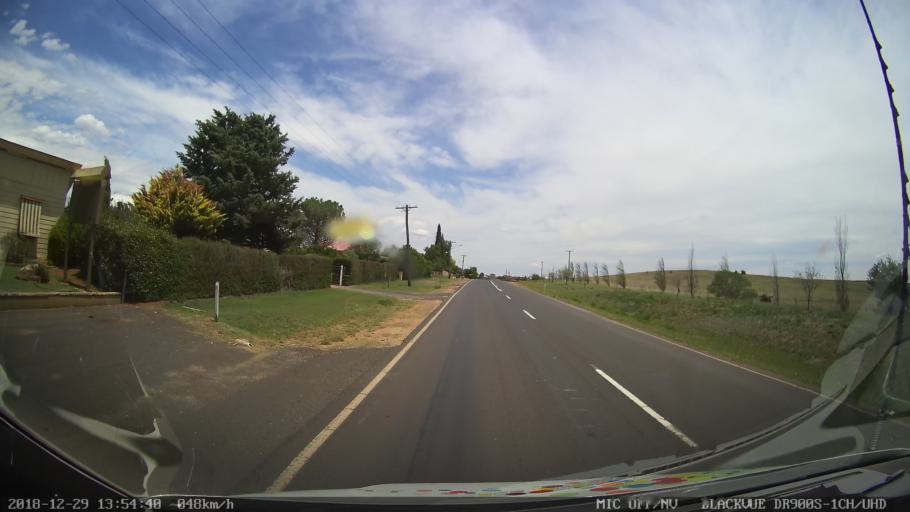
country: AU
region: New South Wales
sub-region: Cooma-Monaro
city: Cooma
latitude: -36.2155
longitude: 149.1511
